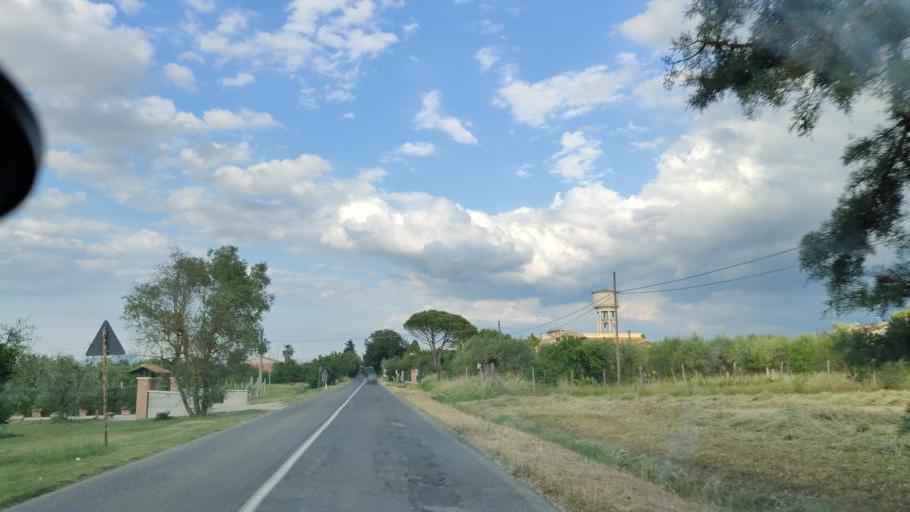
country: IT
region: Umbria
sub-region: Provincia di Terni
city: Giove
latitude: 42.5126
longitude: 12.3462
